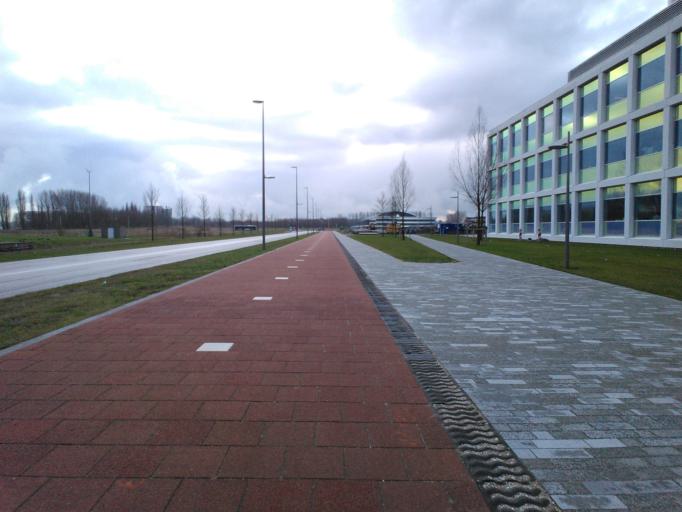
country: NL
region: South Holland
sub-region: Gemeente Delft
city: Delft
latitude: 51.9906
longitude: 4.3806
